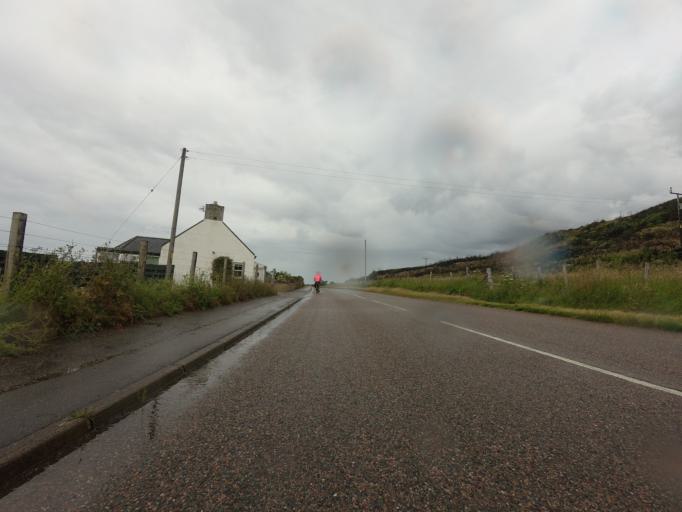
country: GB
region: Scotland
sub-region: Moray
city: Buckie
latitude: 57.6689
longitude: -2.9981
